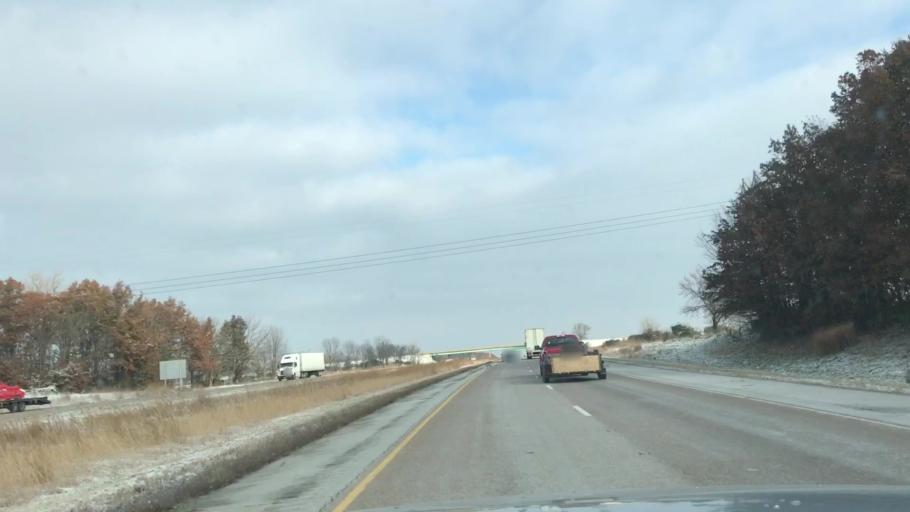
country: US
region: Illinois
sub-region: Macoupin County
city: Mount Olive
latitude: 39.0388
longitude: -89.7554
